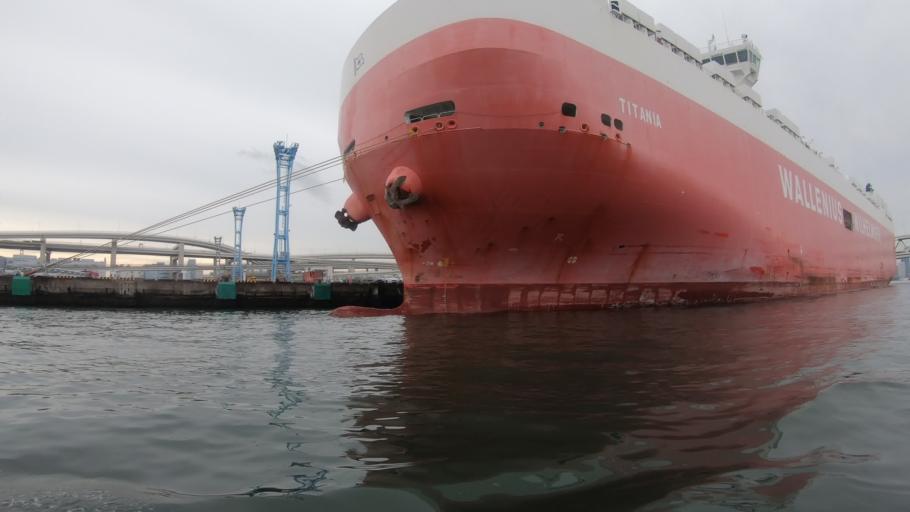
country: JP
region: Kanagawa
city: Yokohama
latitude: 35.4690
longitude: 139.6810
